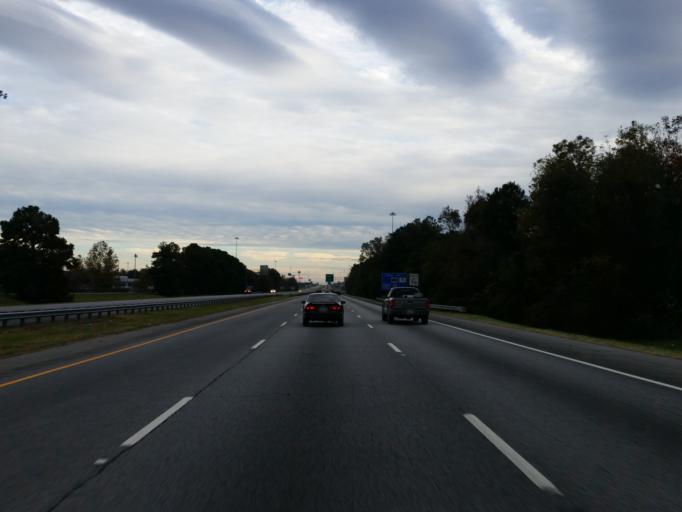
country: US
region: Georgia
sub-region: Lowndes County
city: Remerton
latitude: 30.8383
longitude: -83.3282
